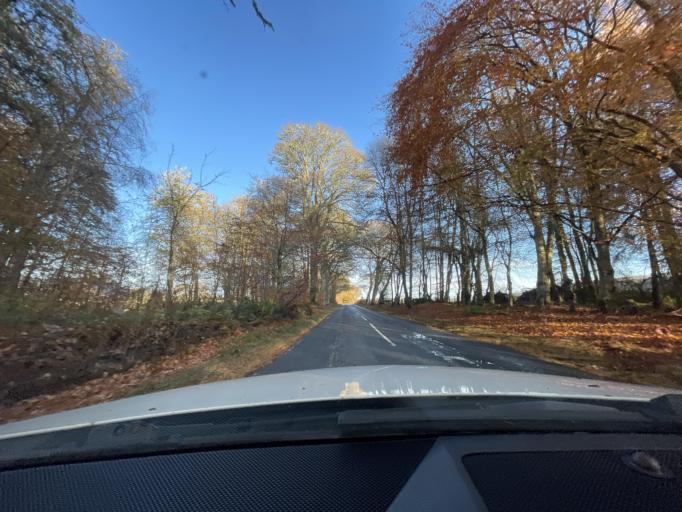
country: GB
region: Scotland
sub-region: Highland
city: Inverness
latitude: 57.4230
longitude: -4.2940
